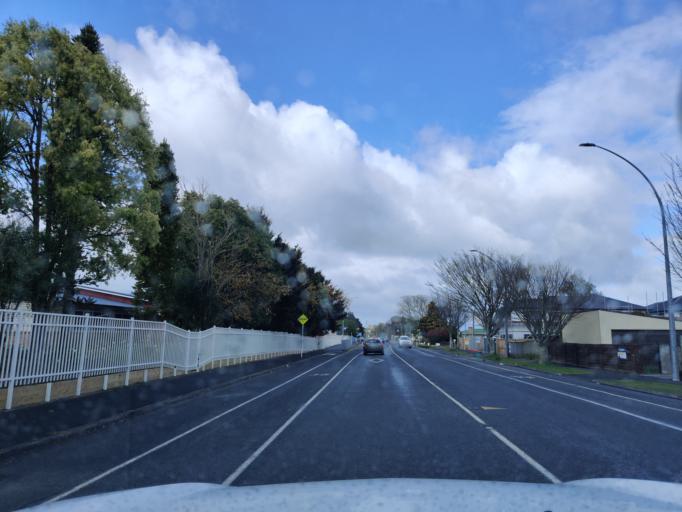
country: NZ
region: Waikato
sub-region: Hamilton City
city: Hamilton
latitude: -37.7919
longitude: 175.2492
